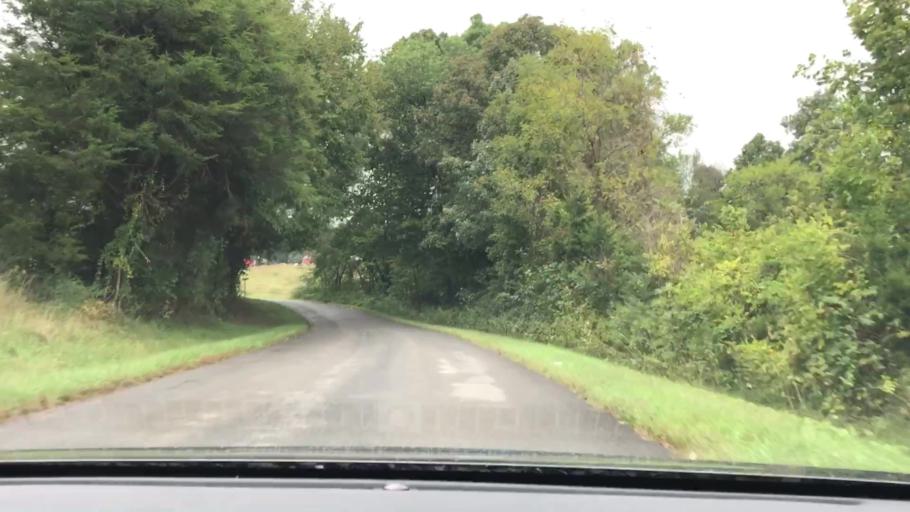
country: US
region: Kentucky
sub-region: Monroe County
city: Tompkinsville
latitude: 36.6200
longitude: -85.7708
